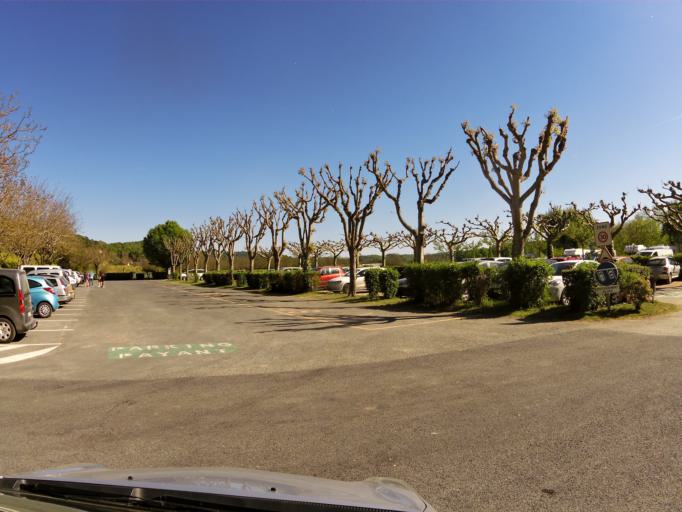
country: FR
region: Aquitaine
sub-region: Departement de la Dordogne
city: Cenac-et-Saint-Julien
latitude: 44.8249
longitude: 1.1842
